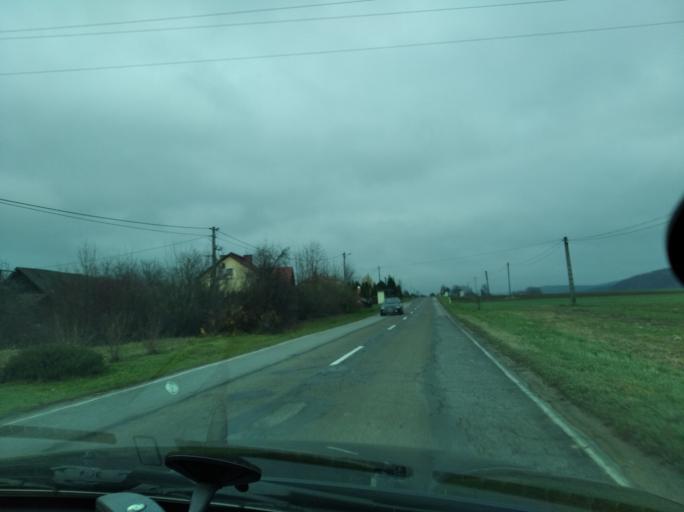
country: PL
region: Subcarpathian Voivodeship
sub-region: Powiat rzeszowski
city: Dynow
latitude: 49.8401
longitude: 22.2435
